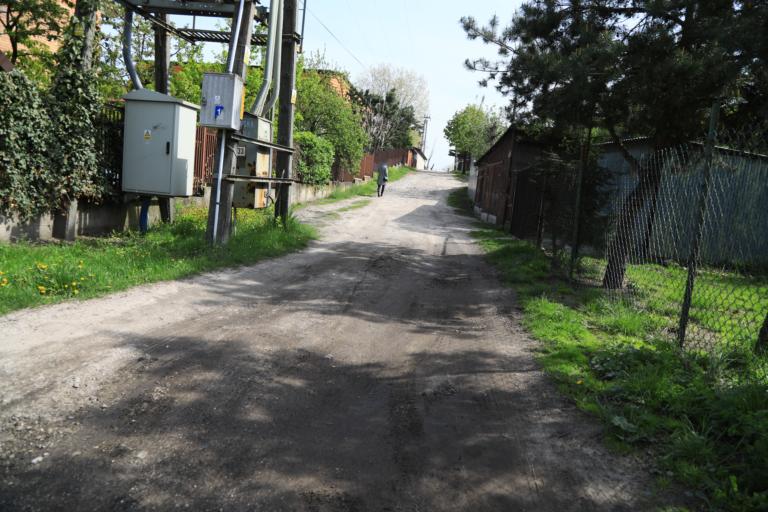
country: PL
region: Masovian Voivodeship
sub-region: Powiat wolominski
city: Wolomin
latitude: 52.3392
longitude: 21.2282
